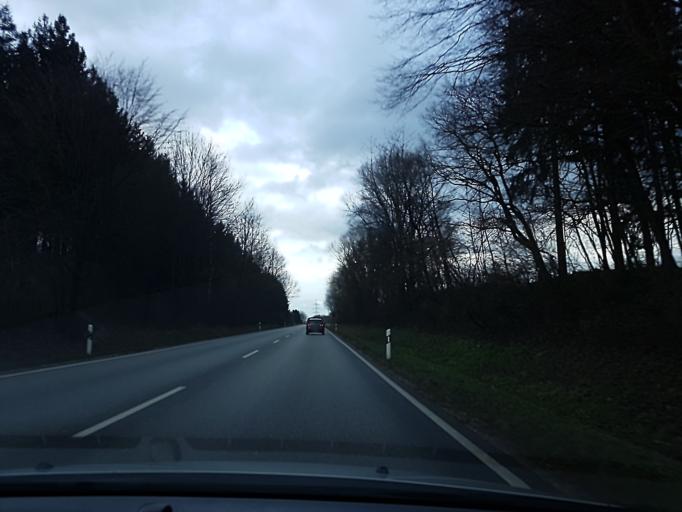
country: DE
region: Bavaria
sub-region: Lower Bavaria
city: Eging
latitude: 48.5000
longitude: 12.2179
